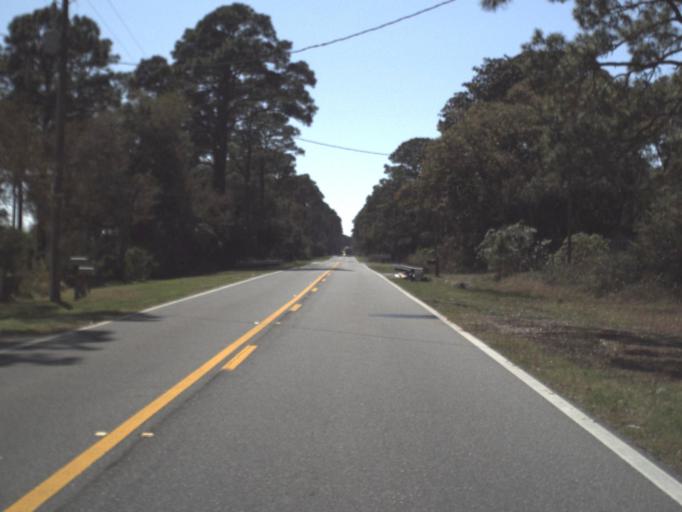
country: US
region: Florida
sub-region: Franklin County
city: Carrabelle
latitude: 29.9053
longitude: -84.5458
